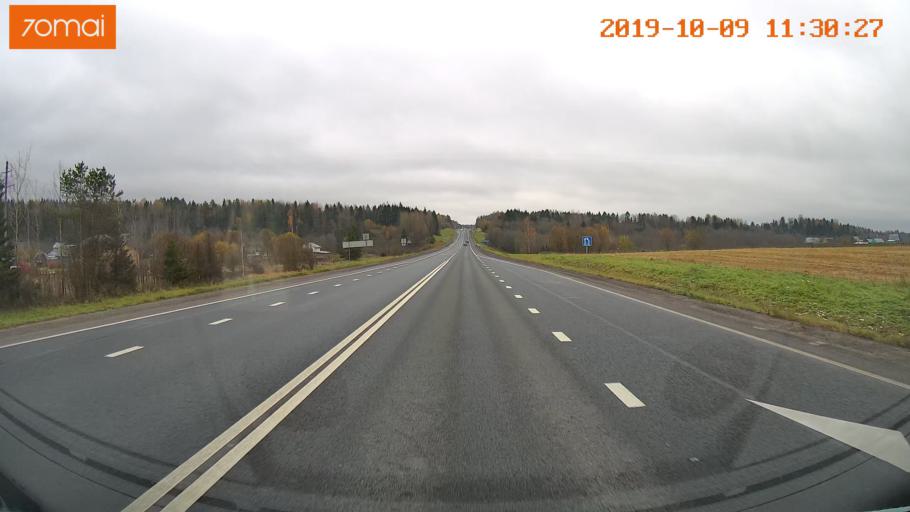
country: RU
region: Vologda
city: Gryazovets
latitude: 59.0536
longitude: 40.0755
